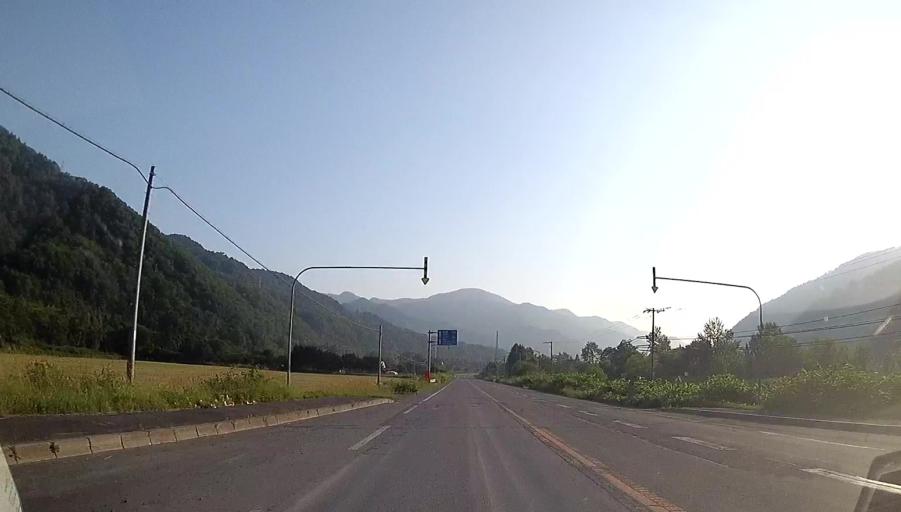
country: JP
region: Hokkaido
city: Shimo-furano
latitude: 42.8971
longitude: 142.5583
